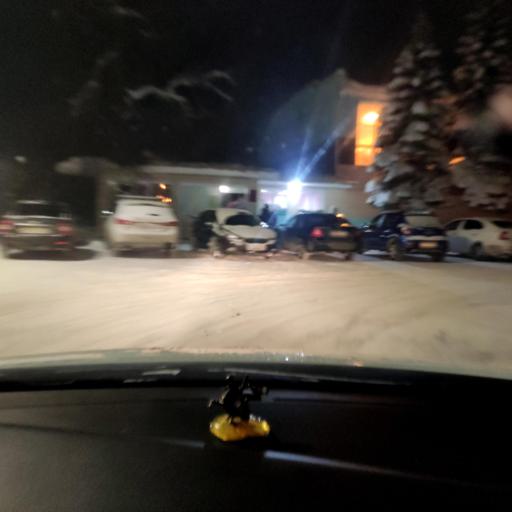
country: RU
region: Tatarstan
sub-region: Zelenodol'skiy Rayon
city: Zelenodolsk
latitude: 55.8458
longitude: 48.4984
